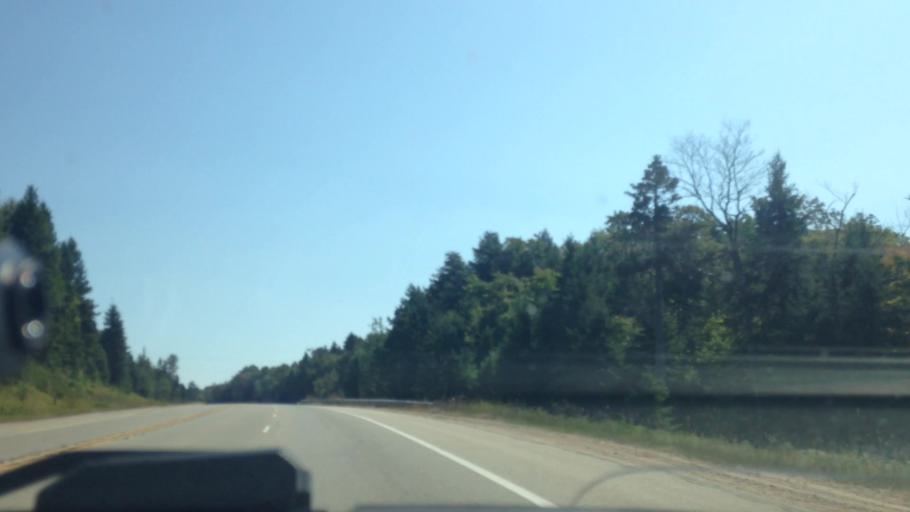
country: US
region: Michigan
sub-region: Alger County
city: Munising
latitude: 46.3882
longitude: -86.6447
